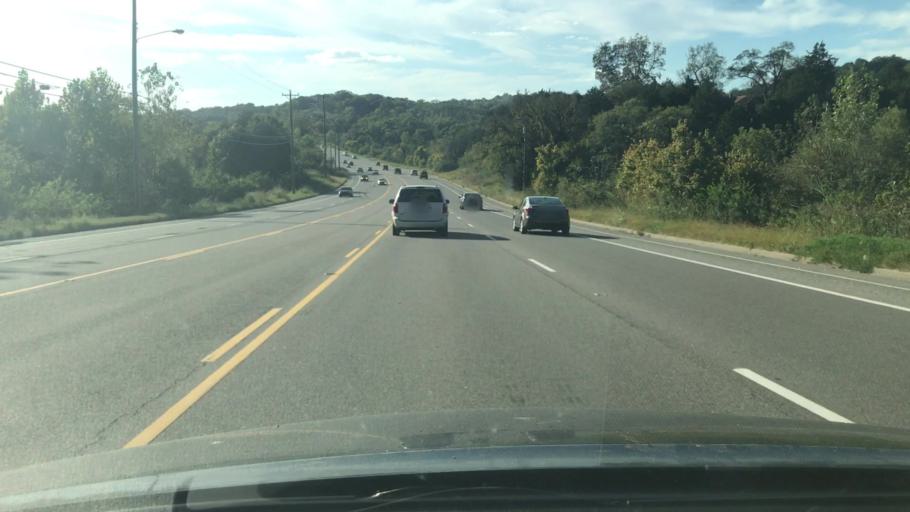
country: US
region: Tennessee
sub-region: Davidson County
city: Nashville
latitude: 36.2111
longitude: -86.8872
